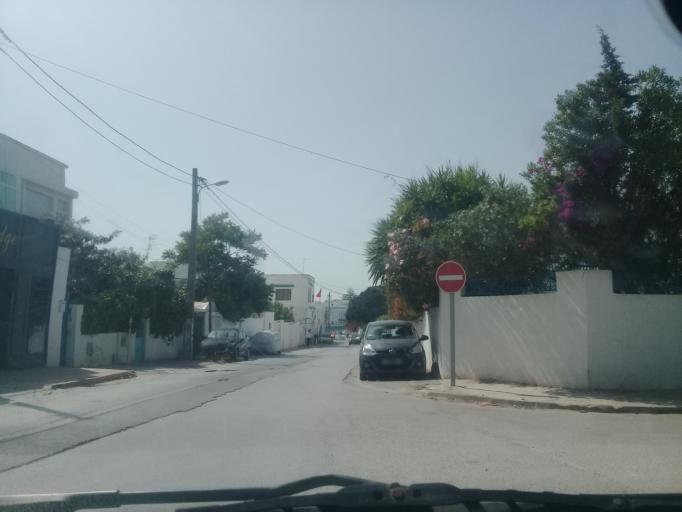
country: TN
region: Tunis
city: Al Marsa
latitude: 36.8818
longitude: 10.3358
